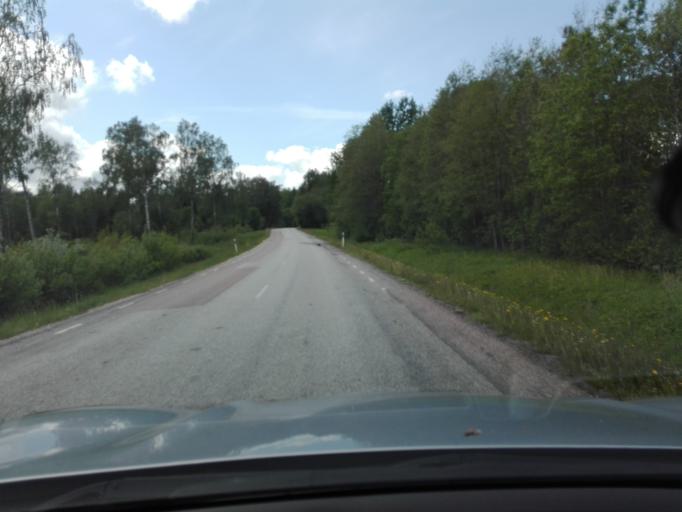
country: EE
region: Raplamaa
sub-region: Rapla vald
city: Rapla
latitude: 59.0163
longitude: 24.8164
